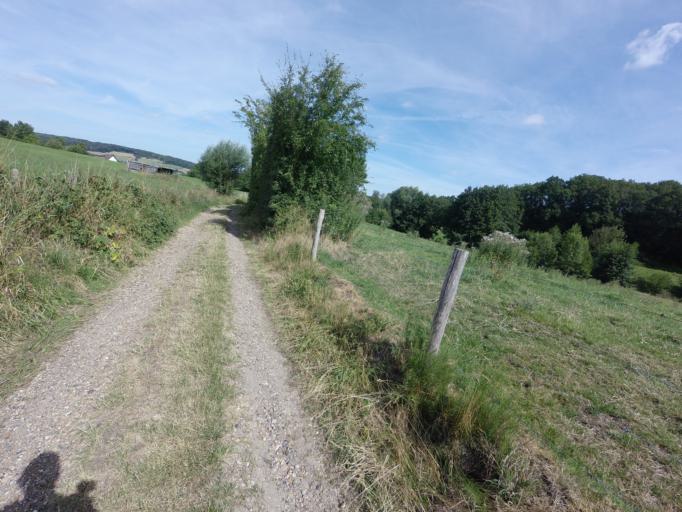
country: BE
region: Wallonia
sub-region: Province de Liege
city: Plombieres
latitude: 50.7796
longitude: 5.9336
